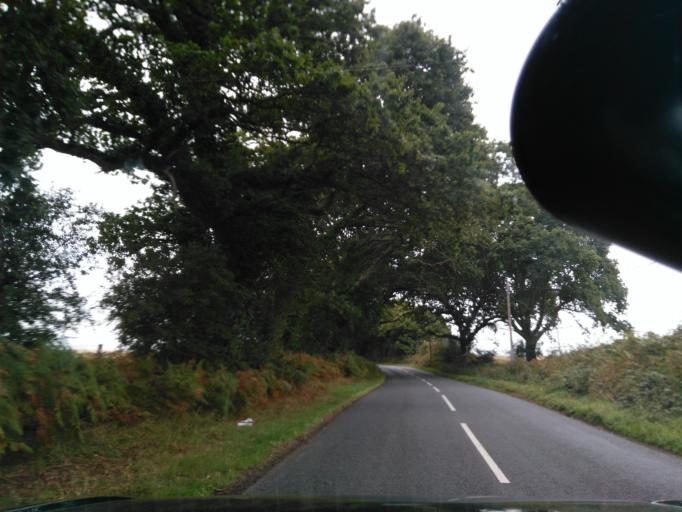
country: GB
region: England
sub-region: Dorset
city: Lytchett Matravers
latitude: 50.7375
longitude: -2.1210
